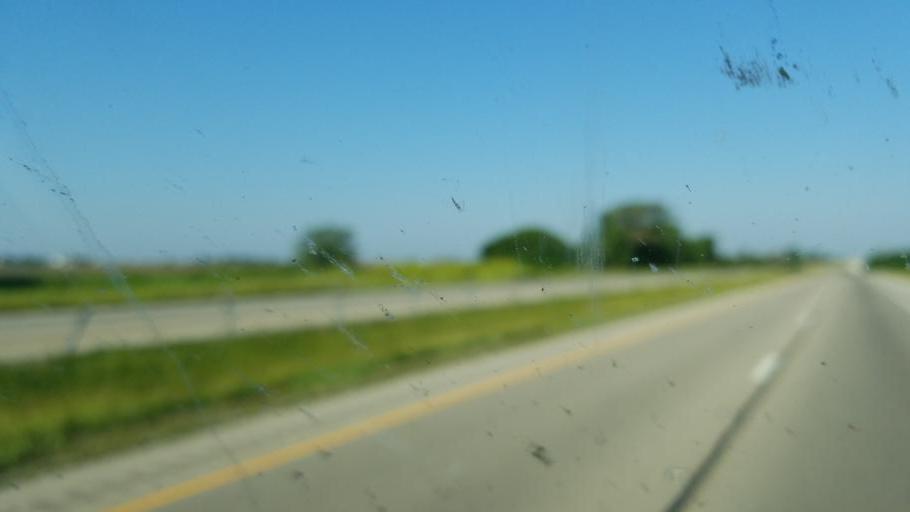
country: US
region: Illinois
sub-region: LaSalle County
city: Marseilles
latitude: 41.3755
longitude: -88.6838
